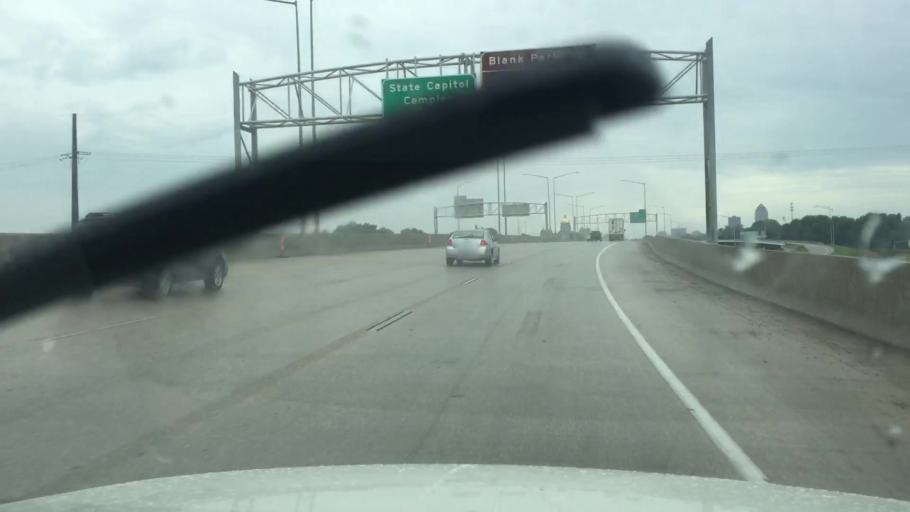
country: US
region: Iowa
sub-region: Polk County
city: Des Moines
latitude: 41.6005
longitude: -93.5860
